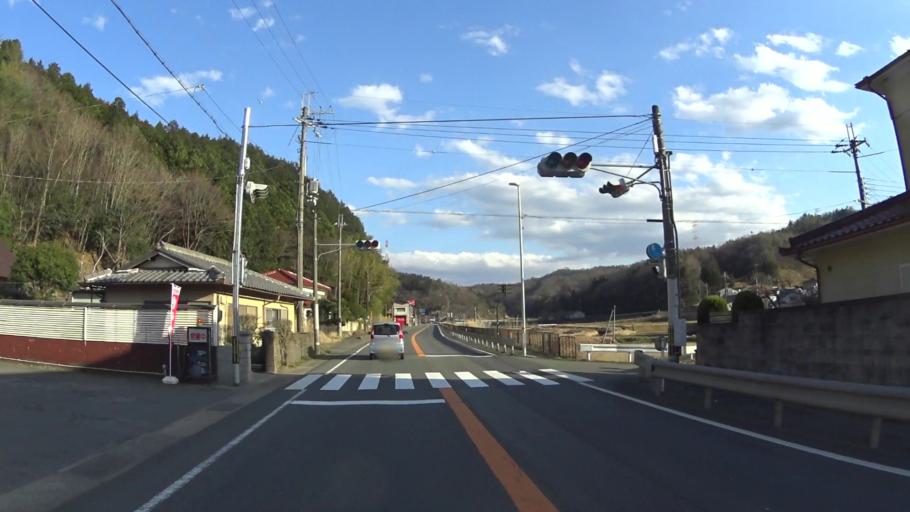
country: JP
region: Kyoto
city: Kameoka
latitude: 35.1234
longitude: 135.4382
